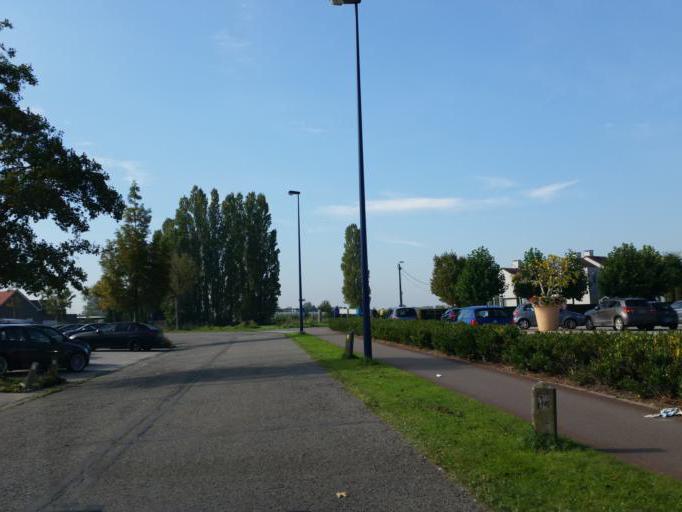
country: BE
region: Flanders
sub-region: Provincie Antwerpen
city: Aartselaar
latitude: 51.1263
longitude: 4.4152
